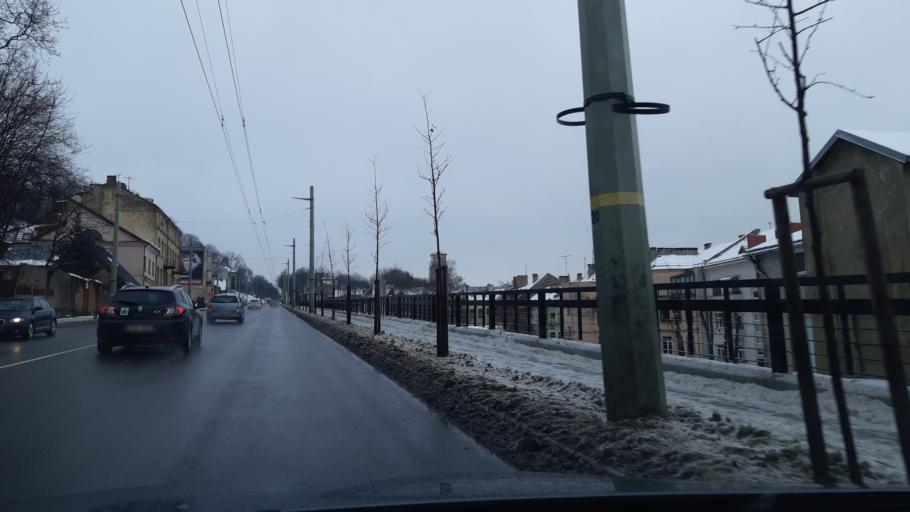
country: LT
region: Kauno apskritis
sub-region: Kaunas
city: Kaunas
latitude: 54.8995
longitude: 23.9044
